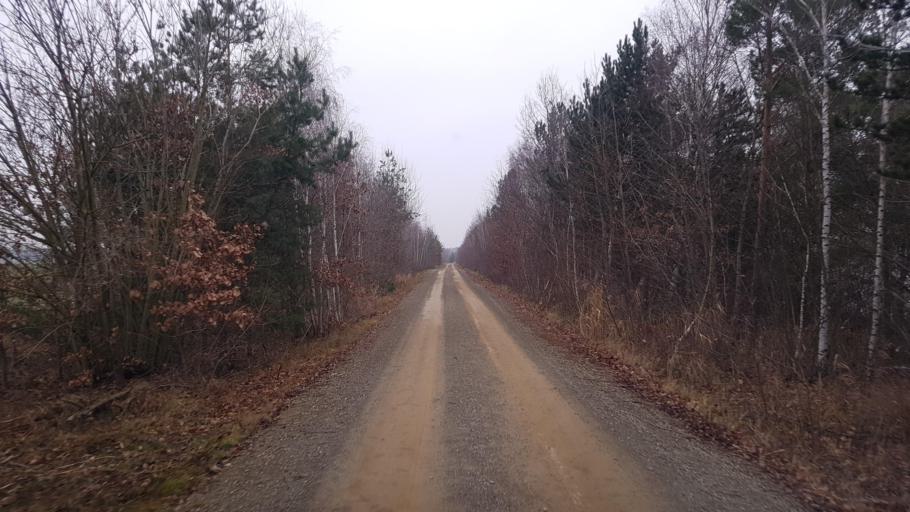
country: DE
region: Brandenburg
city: Plessa
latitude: 51.5073
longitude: 13.6610
